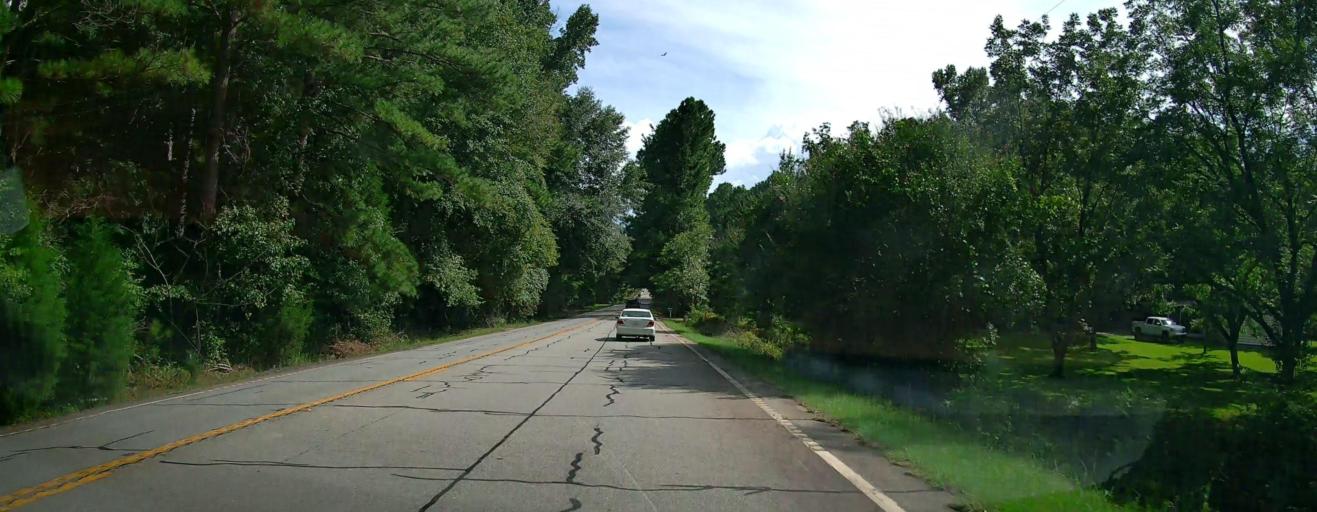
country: US
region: Georgia
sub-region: Harris County
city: Hamilton
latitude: 32.6955
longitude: -84.8566
